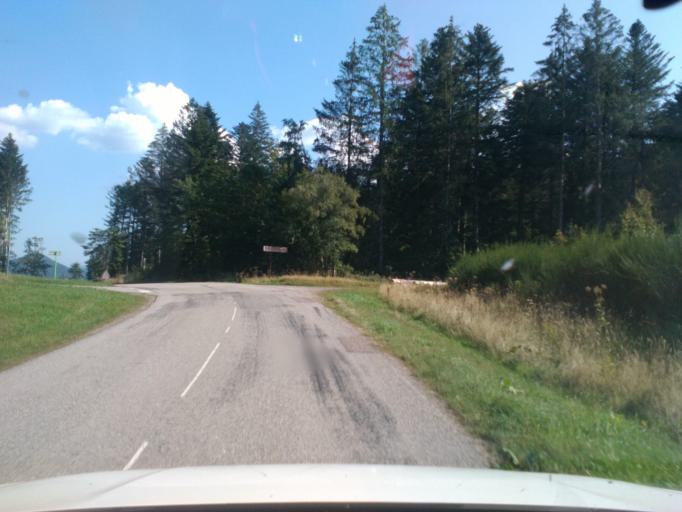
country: FR
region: Lorraine
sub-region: Departement des Vosges
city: Ban-de-Laveline
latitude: 48.3374
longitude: 7.0521
